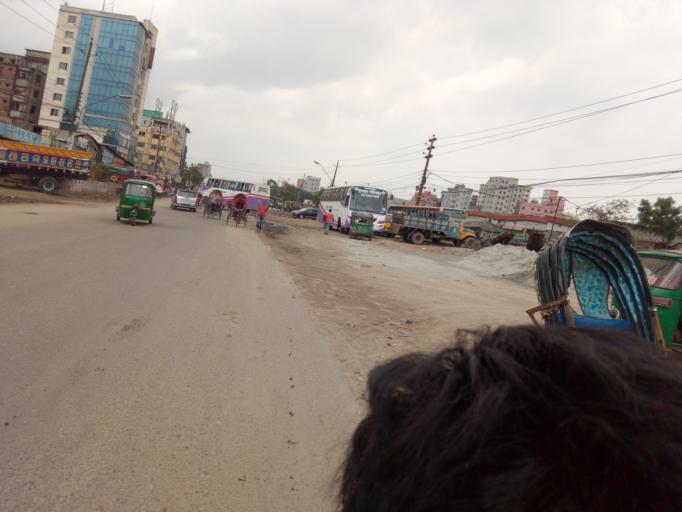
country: BD
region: Dhaka
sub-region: Dhaka
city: Dhaka
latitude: 23.6975
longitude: 90.4358
